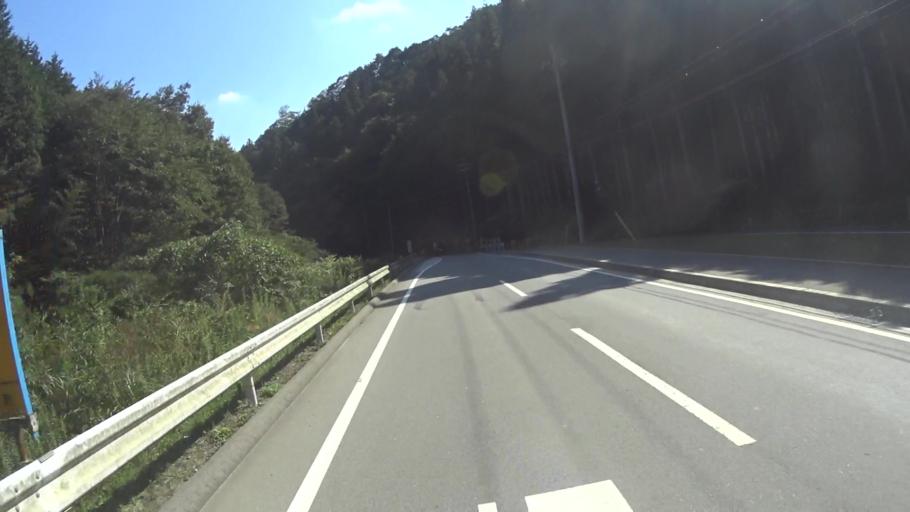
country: JP
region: Kyoto
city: Kameoka
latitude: 34.9596
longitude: 135.5560
